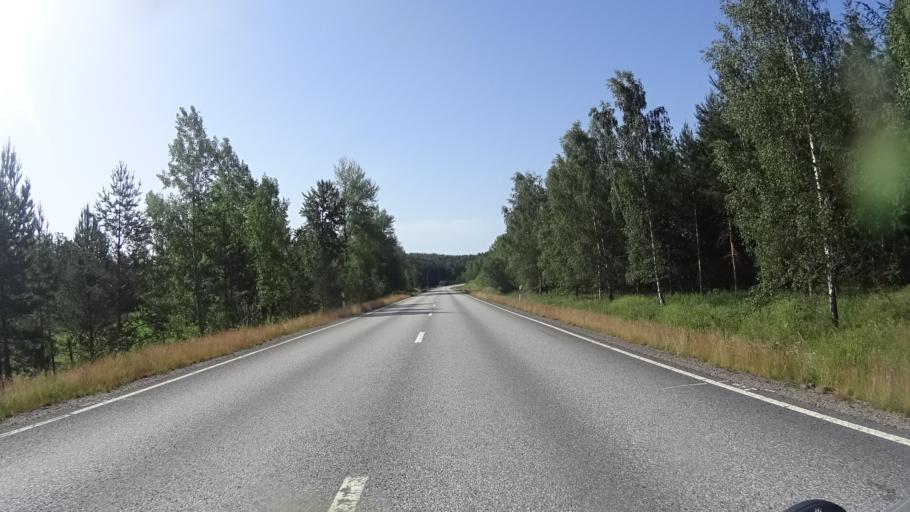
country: SE
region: Kalmar
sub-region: Vasterviks Kommun
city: Overum
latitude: 58.0634
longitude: 16.2035
